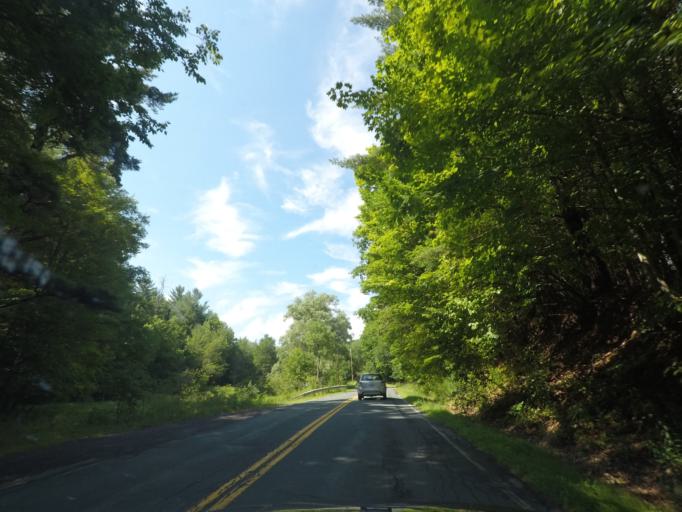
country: US
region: New York
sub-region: Rensselaer County
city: Averill Park
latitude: 42.5757
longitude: -73.5645
